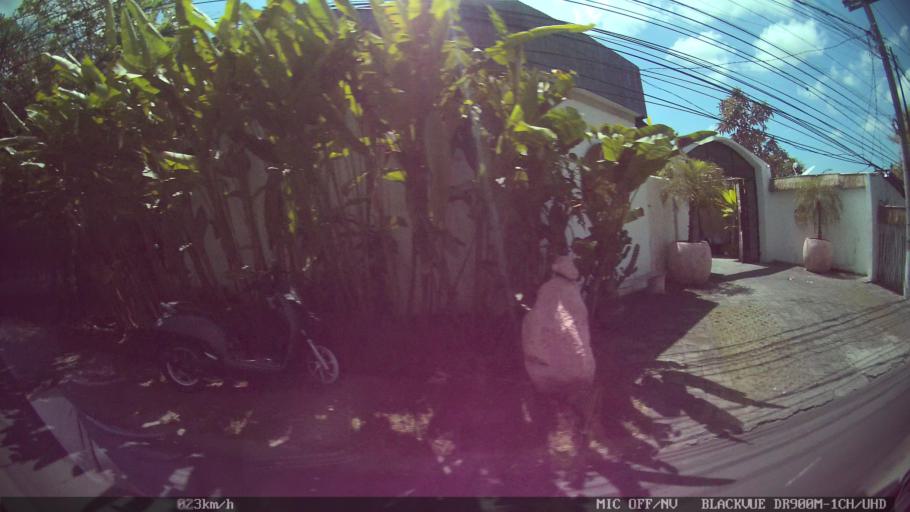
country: ID
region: Bali
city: Banjar Gunungpande
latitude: -8.6643
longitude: 115.1547
